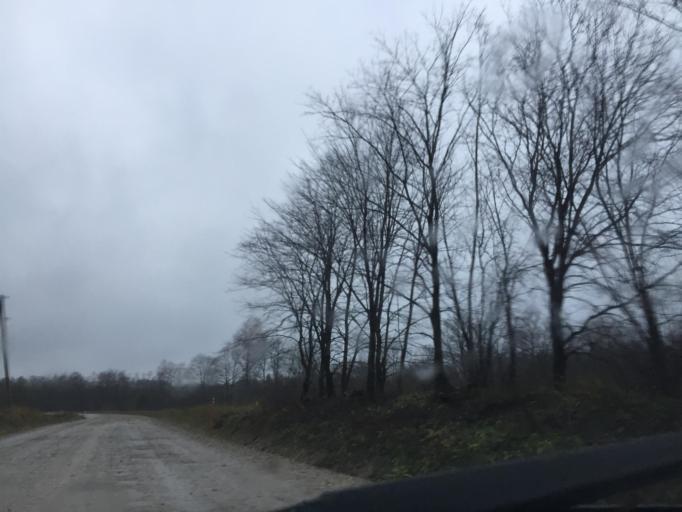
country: LV
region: Salacgrivas
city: Salacgriva
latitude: 57.7628
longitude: 24.4600
